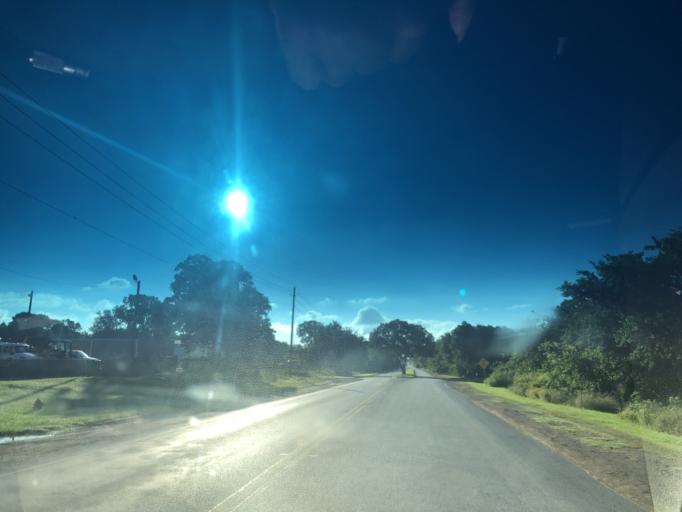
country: US
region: Texas
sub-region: Dallas County
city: Grand Prairie
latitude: 32.7779
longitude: -97.0090
